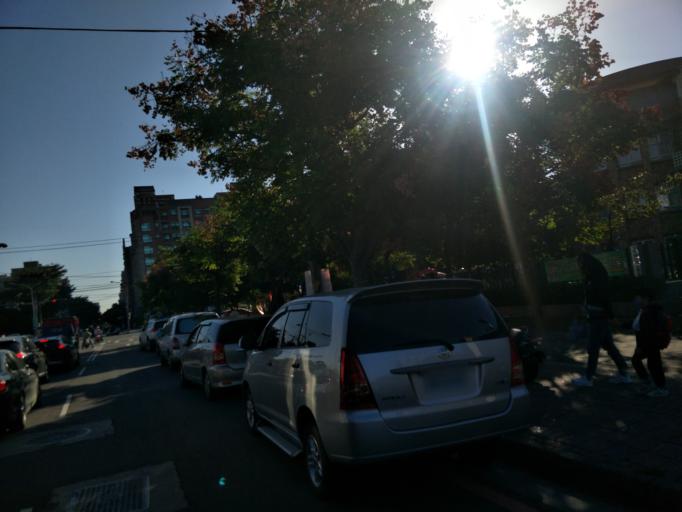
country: TW
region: Taiwan
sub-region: Hsinchu
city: Zhubei
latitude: 24.8362
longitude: 121.0204
